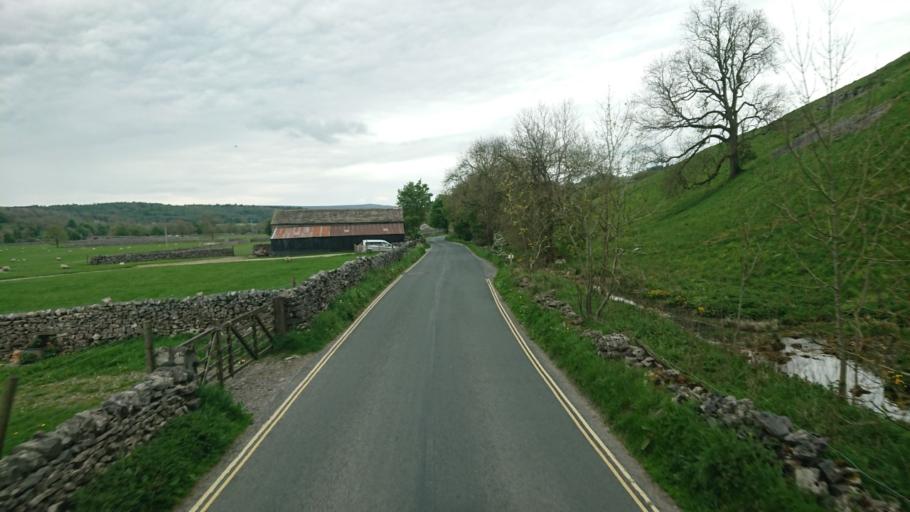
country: GB
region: England
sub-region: North Yorkshire
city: Embsay
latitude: 54.1091
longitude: -2.0400
